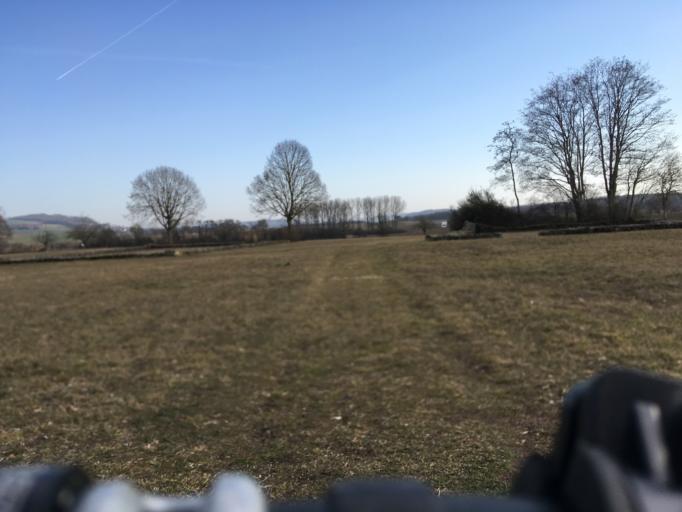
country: CH
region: Schaffhausen
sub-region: Bezirk Reiat
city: Thayngen
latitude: 47.7863
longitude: 8.7036
